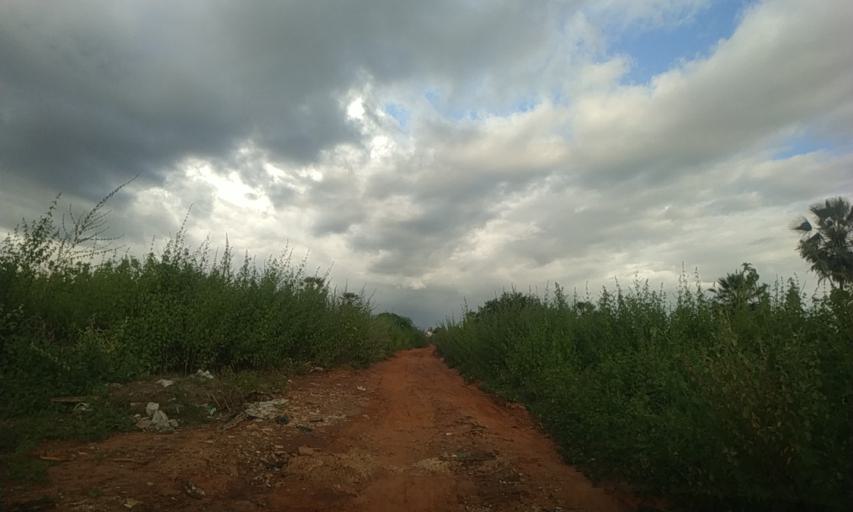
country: BR
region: Rio Grande do Norte
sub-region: Mossoro
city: Mossoro
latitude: -5.2199
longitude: -37.3451
